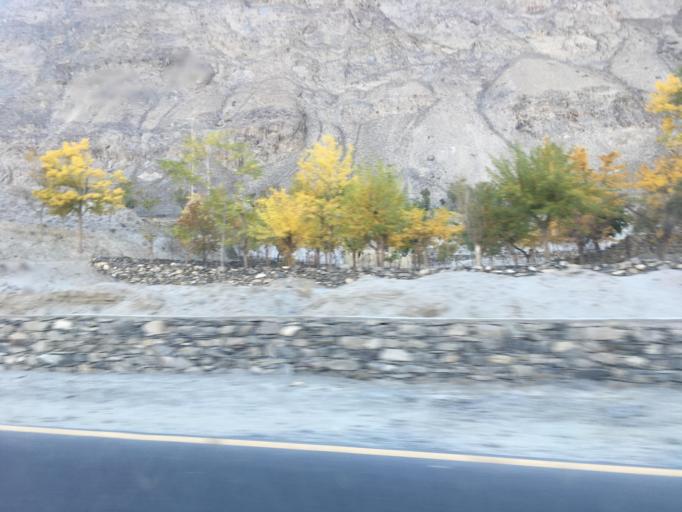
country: PK
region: Gilgit-Baltistan
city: Skardu
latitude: 35.3621
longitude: 75.5059
